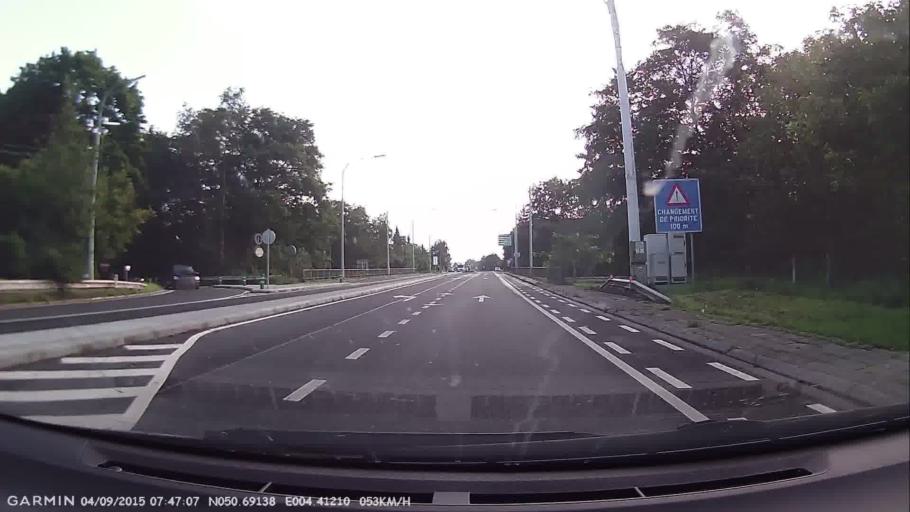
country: BE
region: Wallonia
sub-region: Province du Brabant Wallon
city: Waterloo
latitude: 50.6915
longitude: 4.4124
